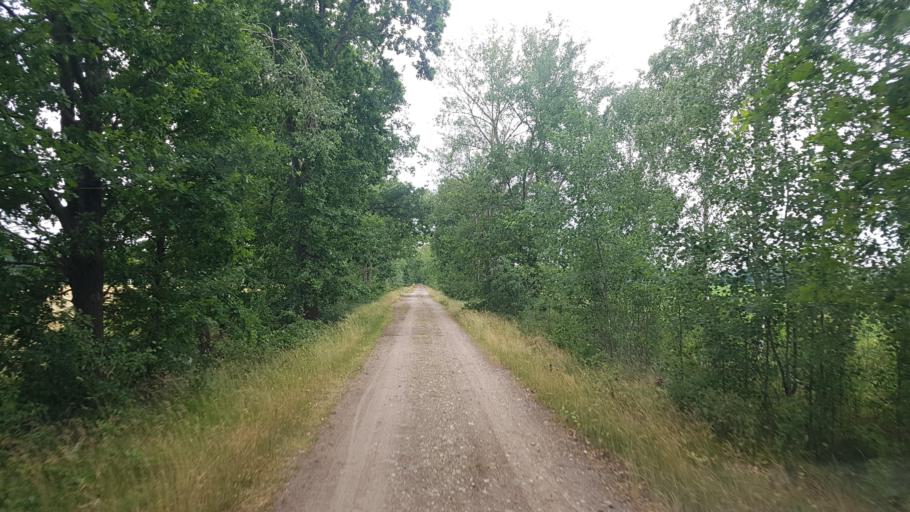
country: DE
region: Brandenburg
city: Schraden
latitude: 51.4159
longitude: 13.6787
